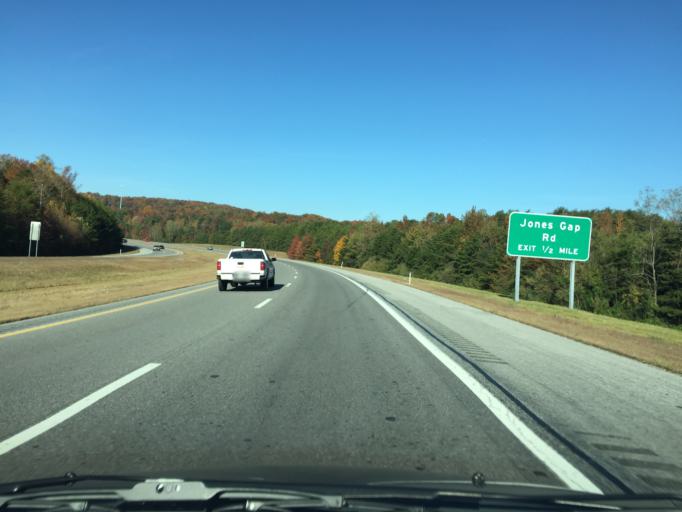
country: US
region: Tennessee
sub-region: Hamilton County
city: Sale Creek
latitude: 35.3440
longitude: -85.1711
